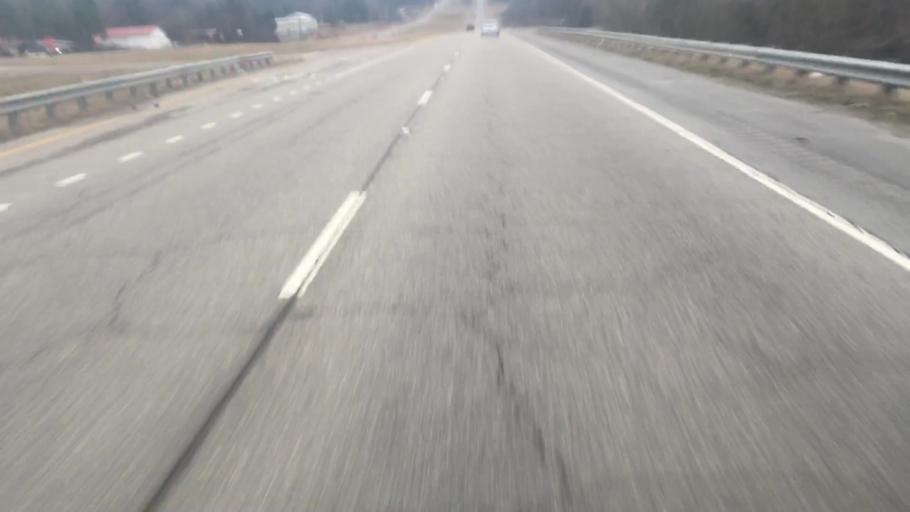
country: US
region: Alabama
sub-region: Walker County
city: Cordova
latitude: 33.8061
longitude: -87.1388
